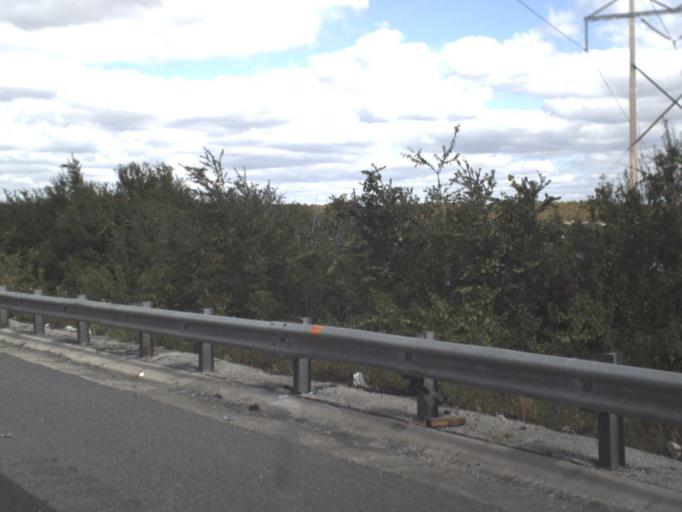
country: US
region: Florida
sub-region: Orange County
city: Meadow Woods
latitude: 28.3543
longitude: -81.3855
